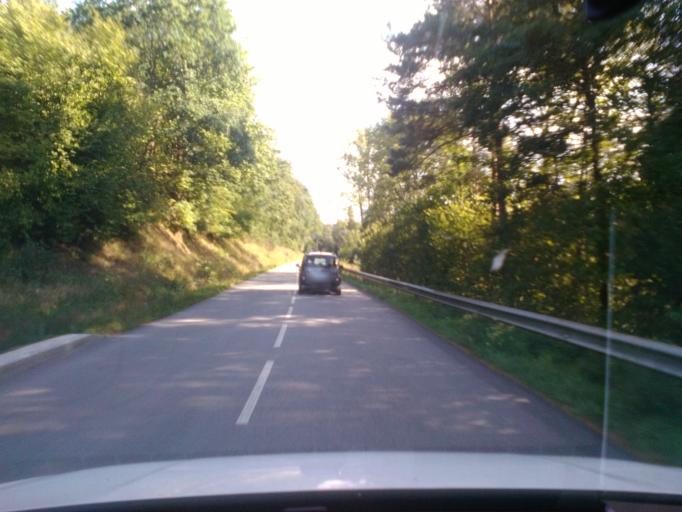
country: FR
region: Lorraine
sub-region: Departement des Vosges
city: Taintrux
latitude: 48.2419
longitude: 6.8934
